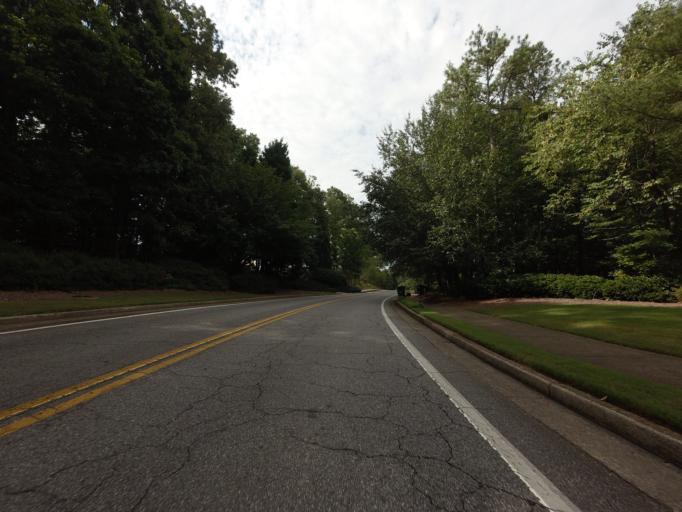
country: US
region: Georgia
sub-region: Gwinnett County
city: Duluth
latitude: 34.0518
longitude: -84.1440
